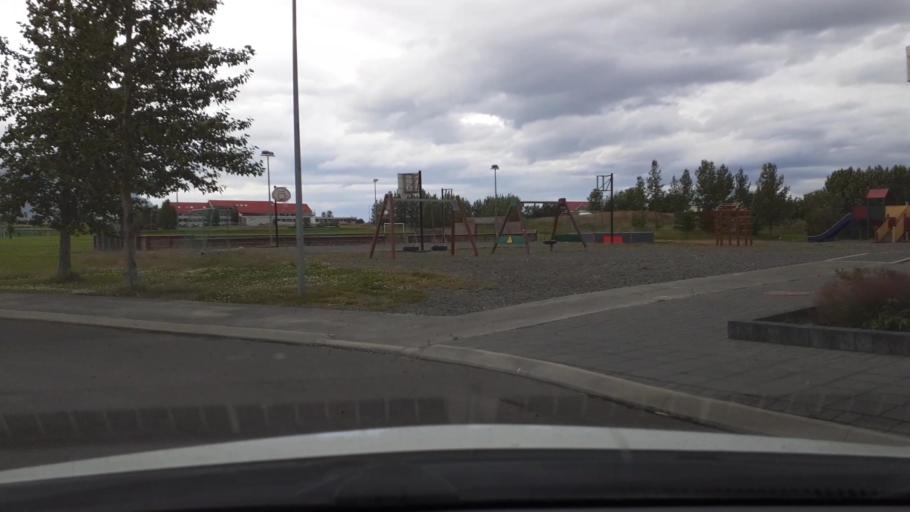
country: IS
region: West
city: Borgarnes
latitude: 64.5630
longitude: -21.7638
